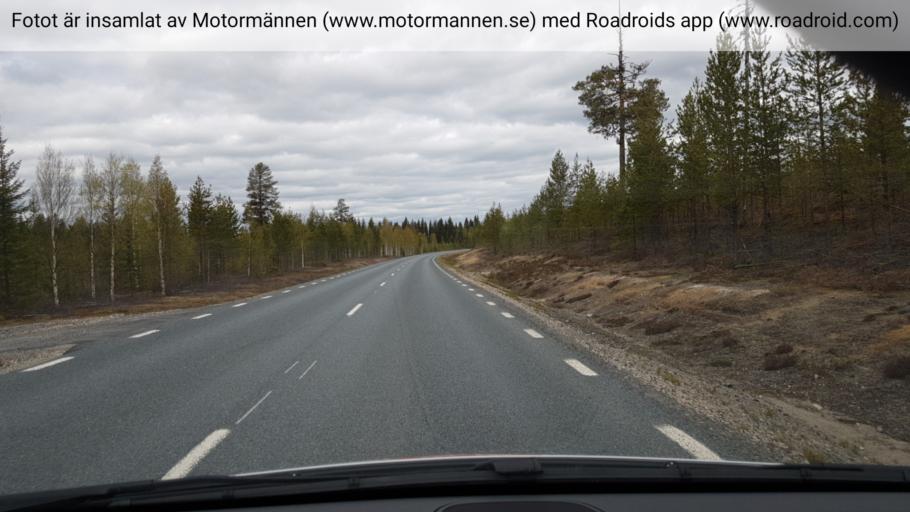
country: SE
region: Vaesterbotten
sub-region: Lycksele Kommun
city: Soderfors
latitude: 65.2174
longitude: 18.1876
